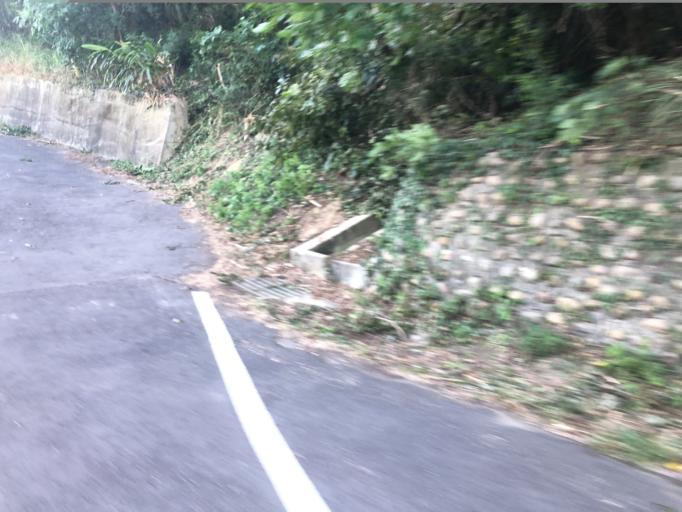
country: TW
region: Taiwan
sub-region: Hsinchu
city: Hsinchu
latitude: 24.7492
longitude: 120.9765
